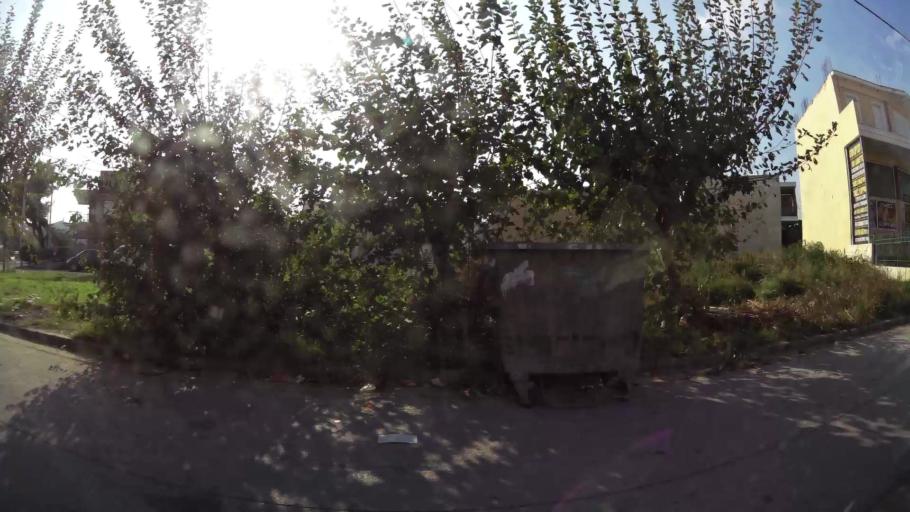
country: GR
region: Attica
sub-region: Nomarchia Anatolikis Attikis
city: Acharnes
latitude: 38.0748
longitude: 23.7292
